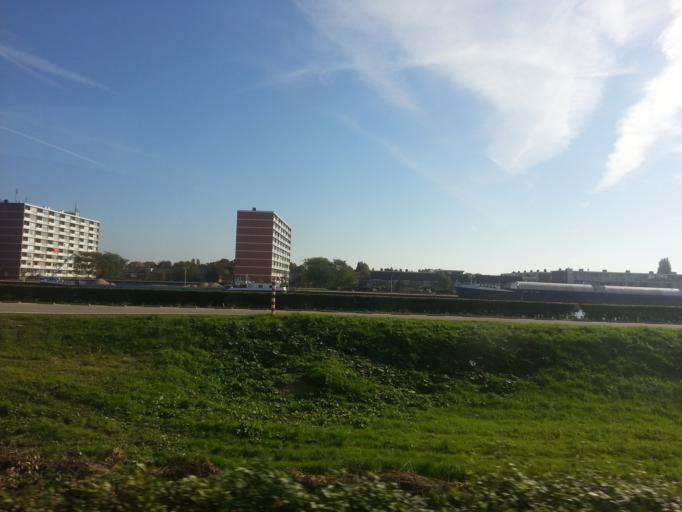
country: NL
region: Utrecht
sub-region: Stichtse Vecht
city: Breukelen
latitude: 52.1825
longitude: 4.9935
